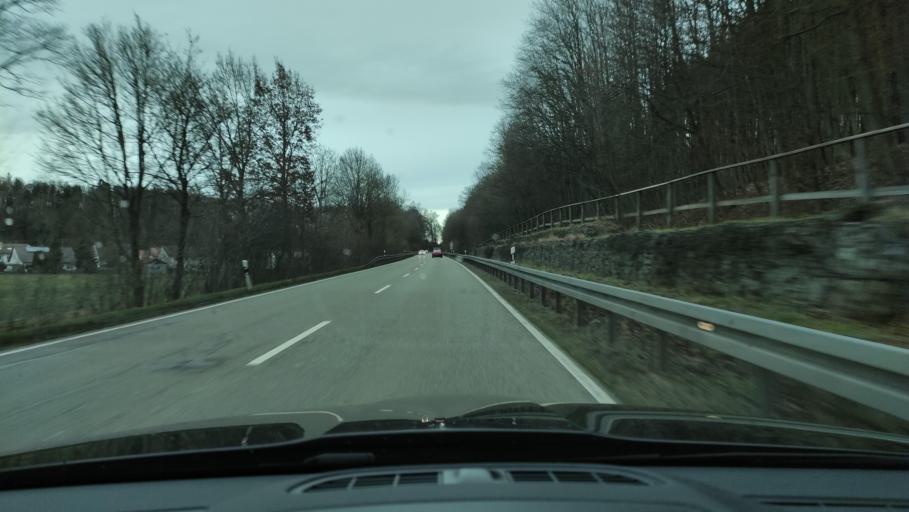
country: DE
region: Bavaria
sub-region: Swabia
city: Illertissen
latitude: 48.2148
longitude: 10.1150
